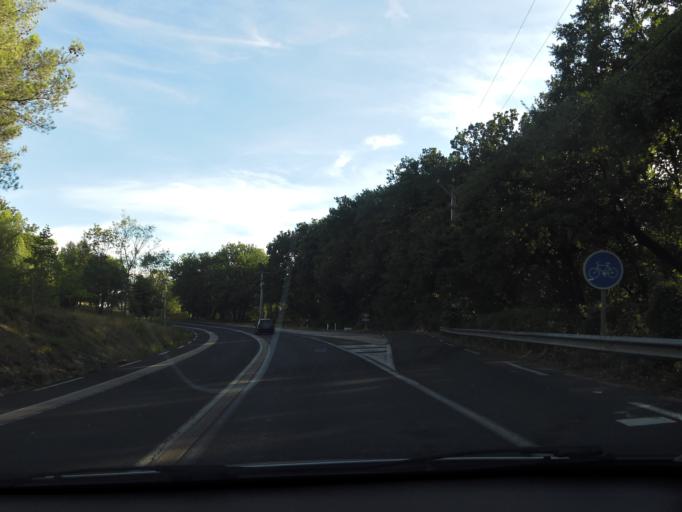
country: FR
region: Languedoc-Roussillon
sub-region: Departement de l'Herault
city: Montferrier-sur-Lez
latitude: 43.6668
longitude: 3.8664
